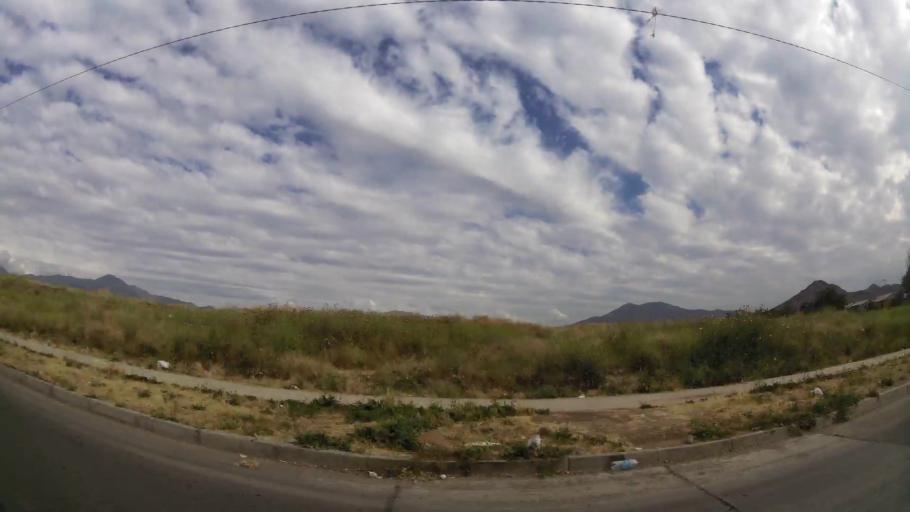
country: CL
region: Santiago Metropolitan
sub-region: Provincia de Santiago
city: La Pintana
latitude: -33.6231
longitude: -70.6192
